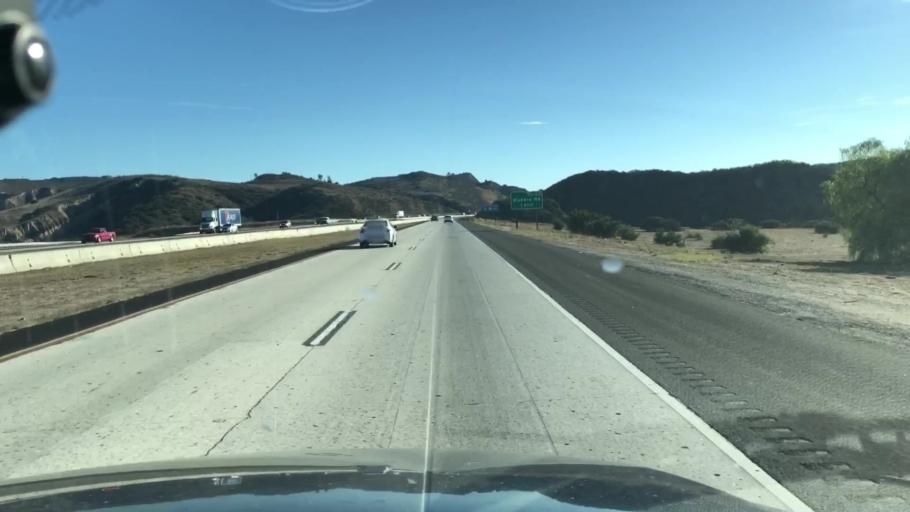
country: US
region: California
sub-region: Ventura County
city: Simi Valley
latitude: 34.2909
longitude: -118.8135
